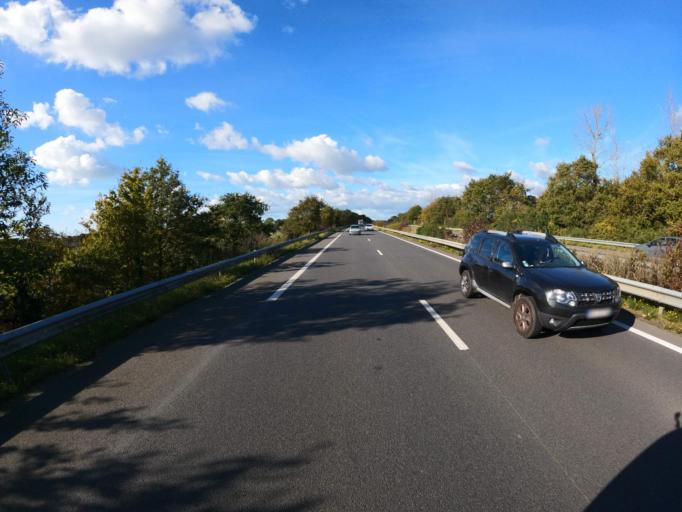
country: FR
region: Pays de la Loire
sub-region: Departement de la Loire-Atlantique
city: Pornichet
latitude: 47.2885
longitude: -2.3270
